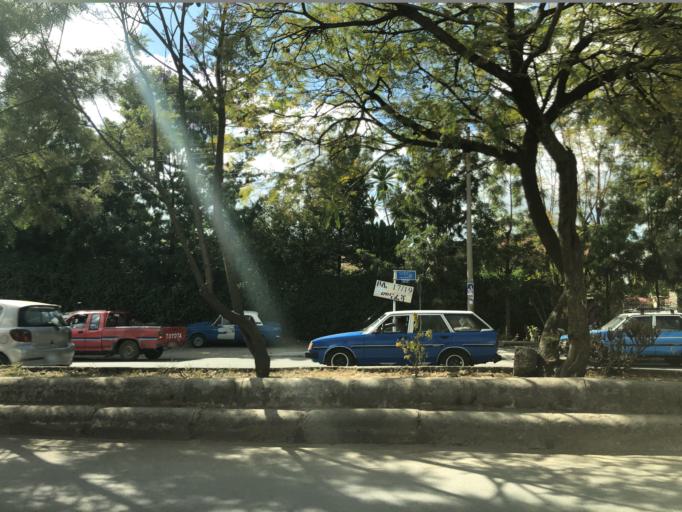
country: ET
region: Adis Abeba
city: Addis Ababa
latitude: 8.9967
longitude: 38.7789
